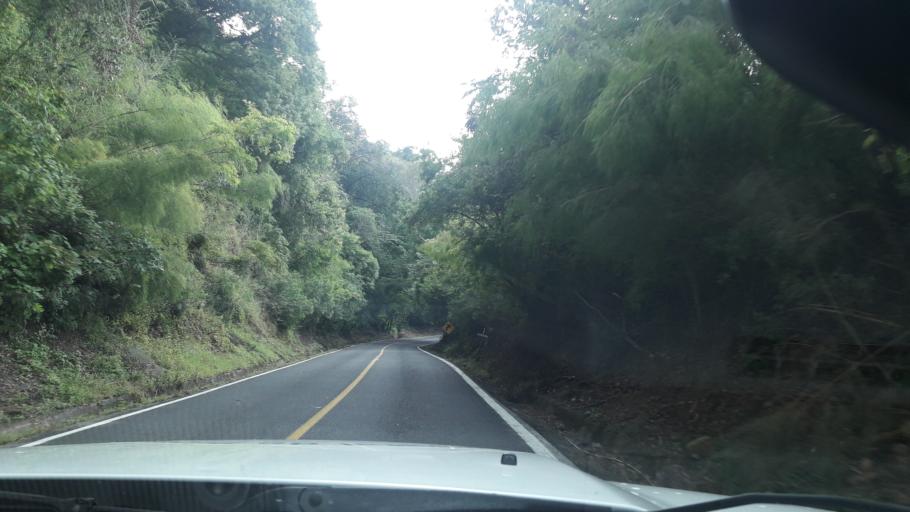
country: MX
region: Colima
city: Suchitlan
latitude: 19.4491
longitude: -103.7183
